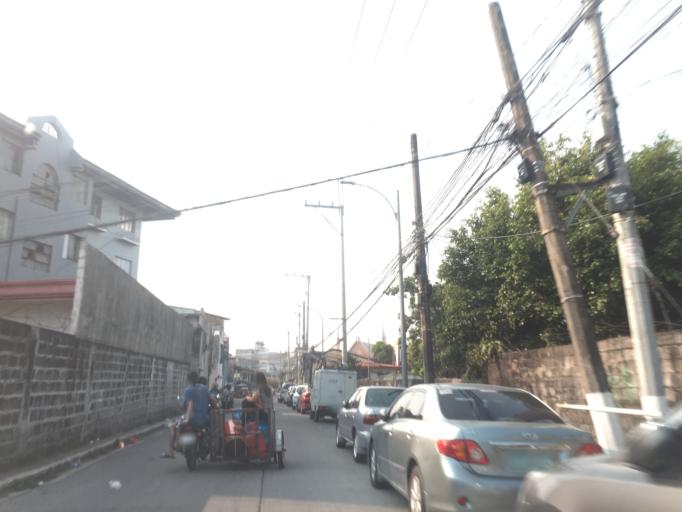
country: PH
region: Calabarzon
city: Bagong Pagasa
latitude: 14.6628
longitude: 121.0184
